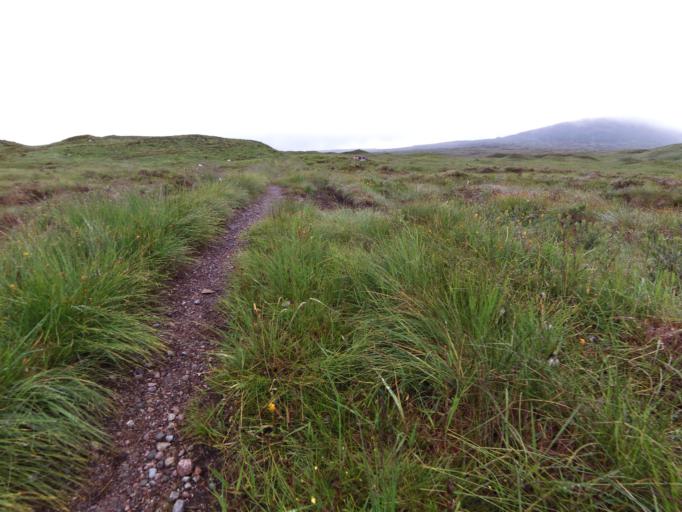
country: GB
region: Scotland
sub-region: Highland
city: Spean Bridge
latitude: 56.7674
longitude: -4.7034
